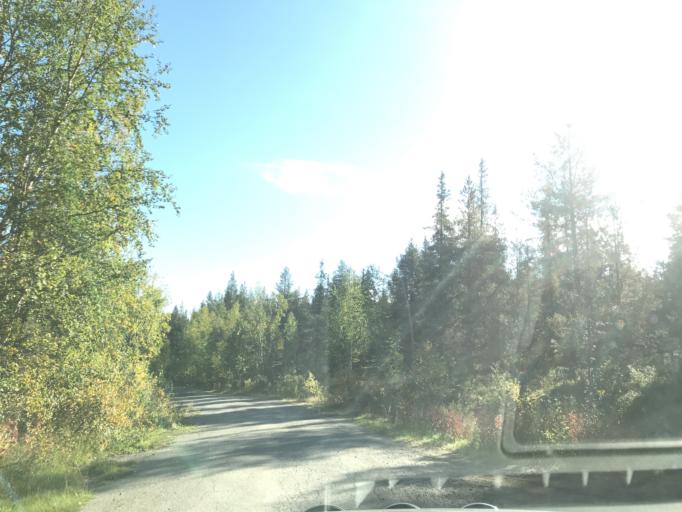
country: SE
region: Norrbotten
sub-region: Gallivare Kommun
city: Malmberget
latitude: 67.6465
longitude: 21.0725
